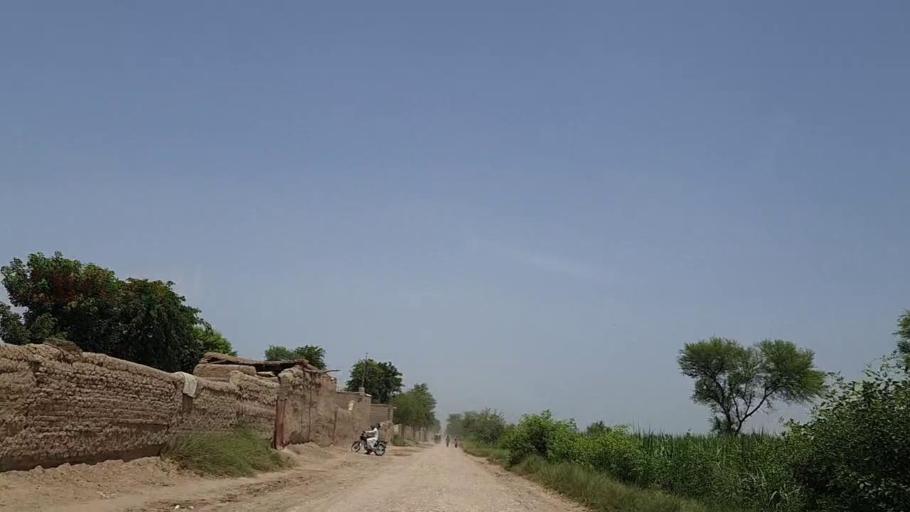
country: PK
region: Sindh
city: Tharu Shah
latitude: 26.9019
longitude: 68.0071
